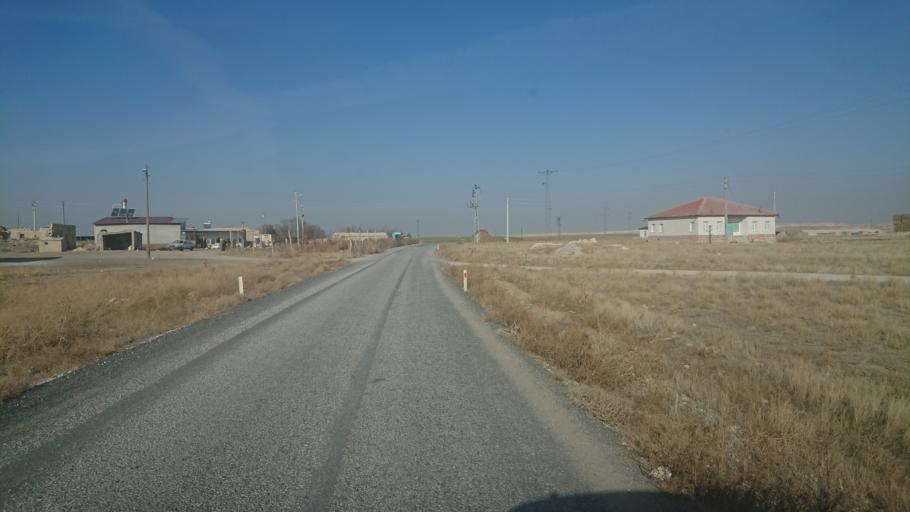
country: TR
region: Aksaray
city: Sultanhani
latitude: 38.0370
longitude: 33.6061
